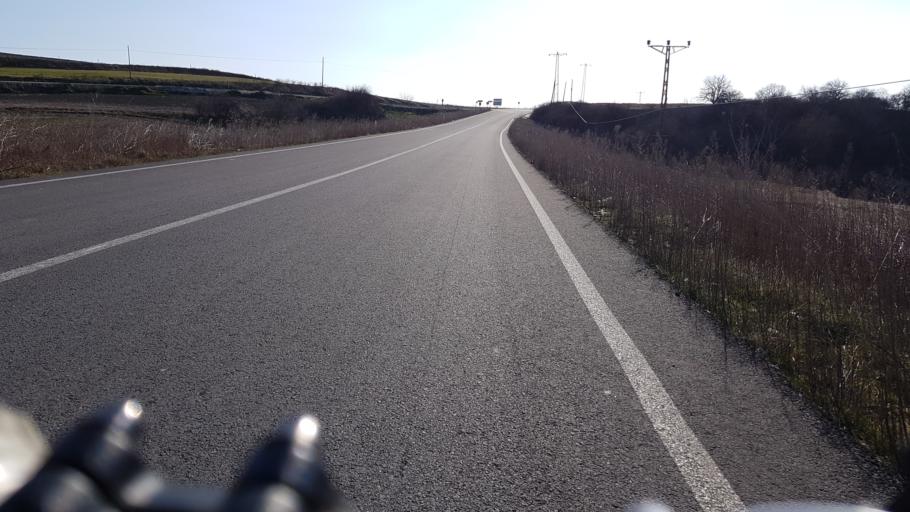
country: TR
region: Tekirdag
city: Velimese
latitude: 41.3564
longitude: 27.8499
